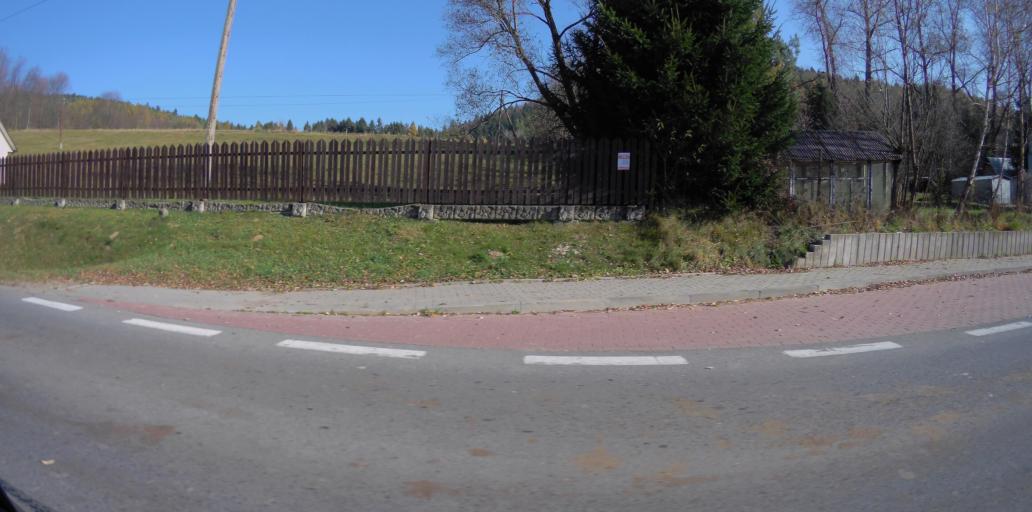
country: PL
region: Subcarpathian Voivodeship
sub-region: Powiat bieszczadzki
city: Ustrzyki Dolne
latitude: 49.4844
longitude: 22.6626
